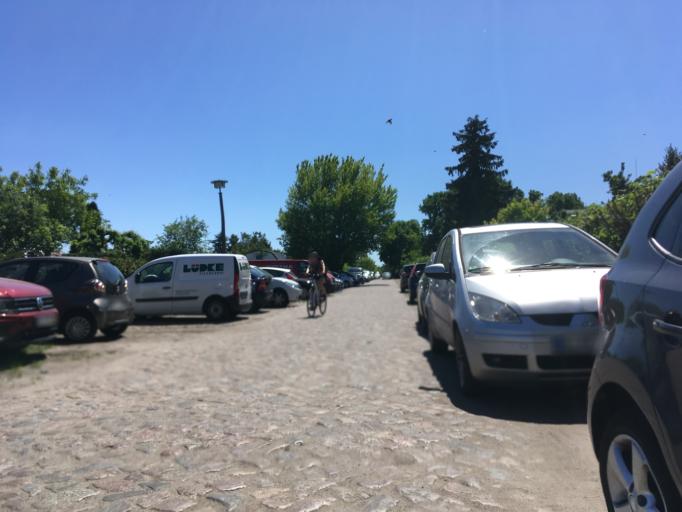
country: DE
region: Berlin
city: Baumschulenweg
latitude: 52.4771
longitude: 13.5008
